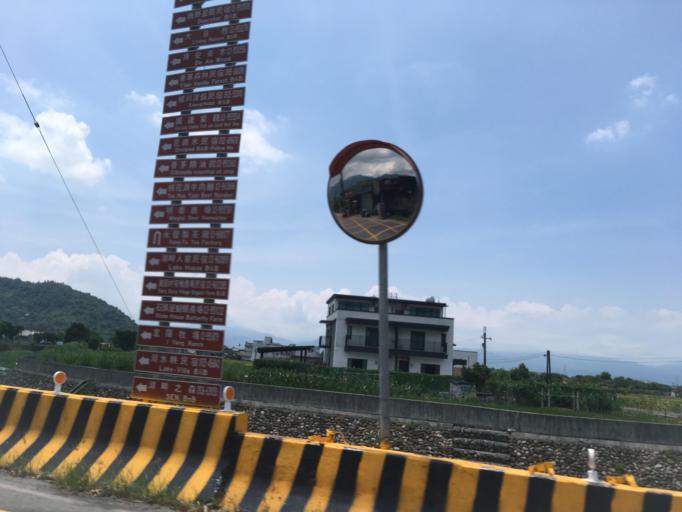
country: TW
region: Taiwan
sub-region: Yilan
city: Yilan
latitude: 24.6398
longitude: 121.7571
